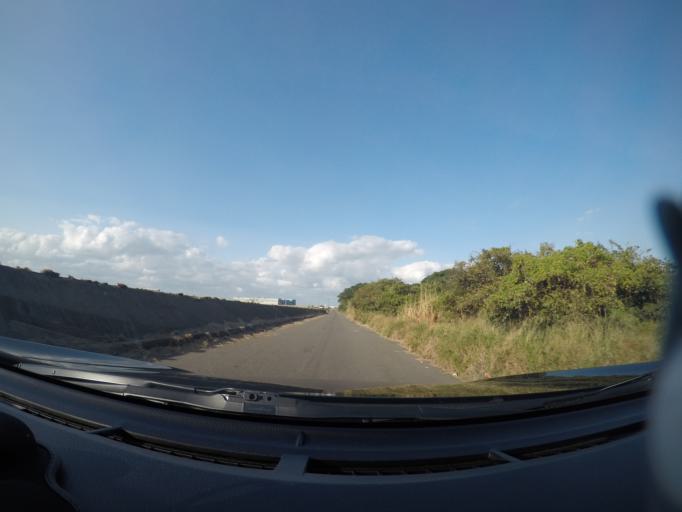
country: TW
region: Taiwan
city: Taoyuan City
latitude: 25.1002
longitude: 121.2516
